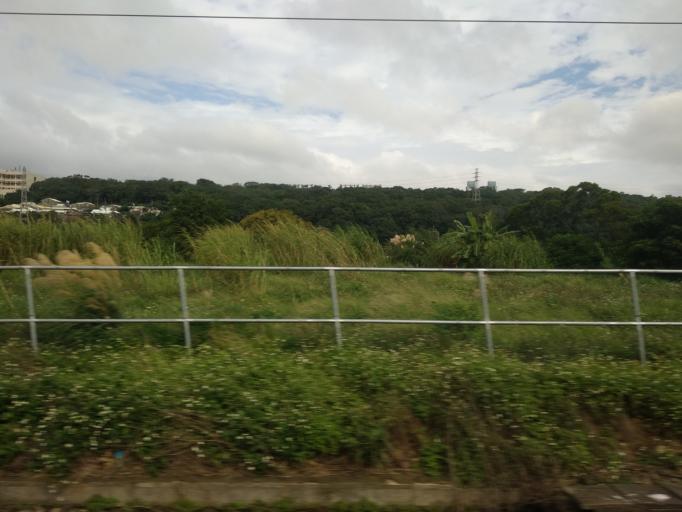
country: TW
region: Taiwan
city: Daxi
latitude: 24.9138
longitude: 121.1579
